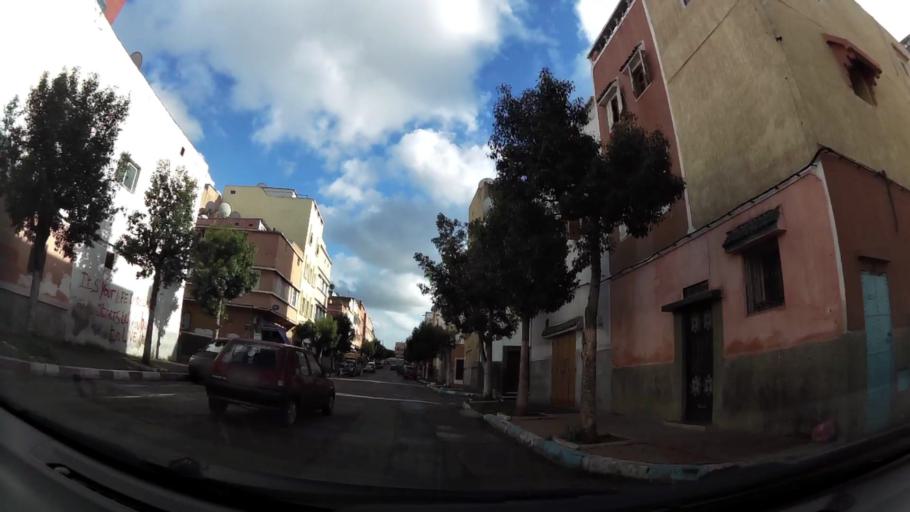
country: MA
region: Grand Casablanca
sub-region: Casablanca
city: Casablanca
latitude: 33.5515
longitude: -7.5949
